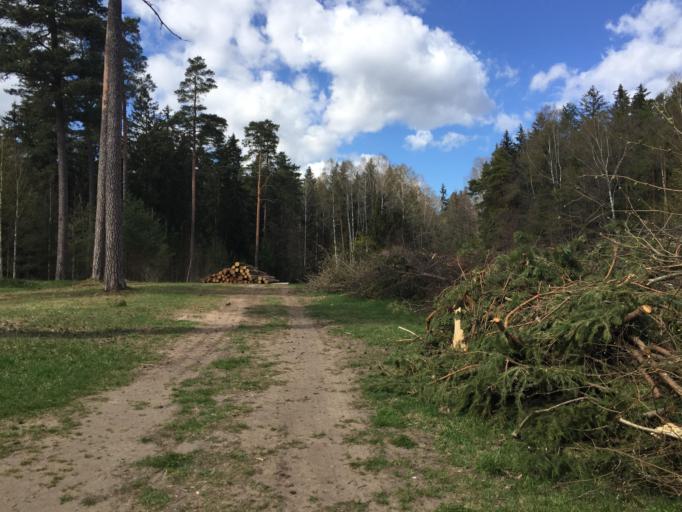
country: LV
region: Baldone
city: Baldone
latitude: 56.7467
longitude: 24.3838
